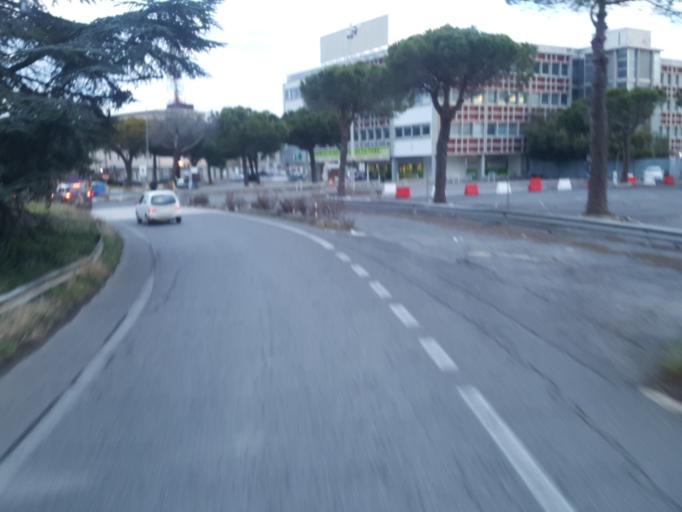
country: IT
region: Latium
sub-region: Citta metropolitana di Roma Capitale
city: Area Produttiva
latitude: 41.6765
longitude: 12.5005
